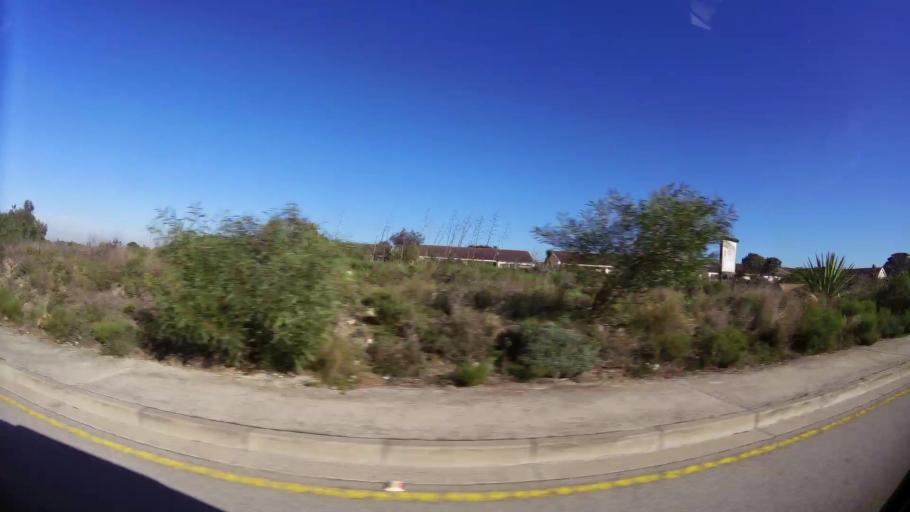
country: ZA
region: Eastern Cape
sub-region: Nelson Mandela Bay Metropolitan Municipality
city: Port Elizabeth
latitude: -33.9790
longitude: 25.6347
